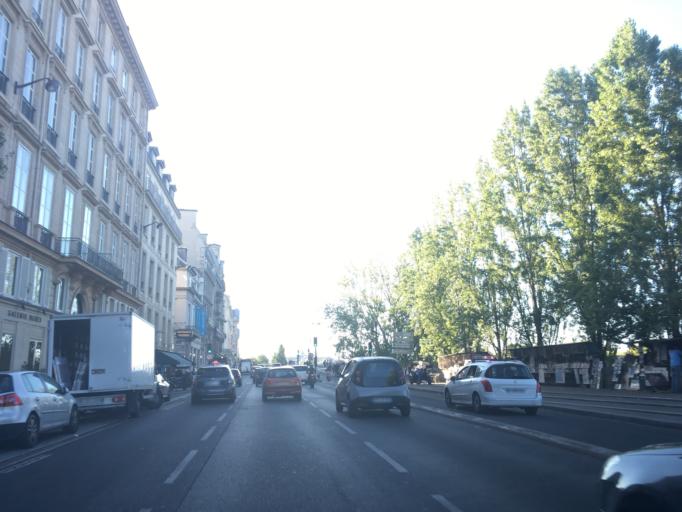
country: FR
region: Ile-de-France
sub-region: Paris
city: Paris
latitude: 48.8590
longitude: 2.3310
